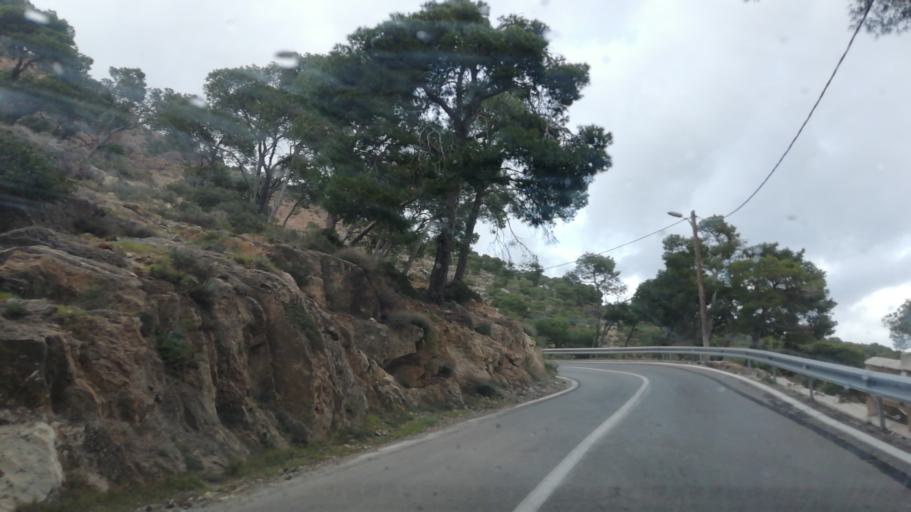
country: DZ
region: Oran
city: Oran
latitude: 35.7053
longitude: -0.6639
